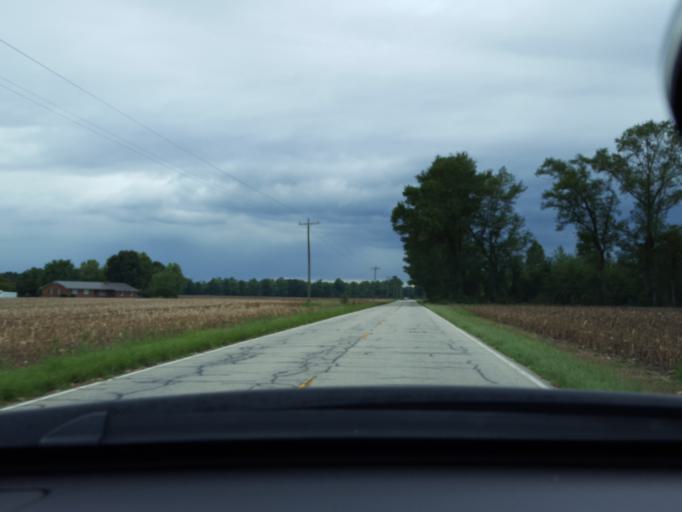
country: US
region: North Carolina
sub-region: Duplin County
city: Rose Hill
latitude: 34.8180
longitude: -78.1769
